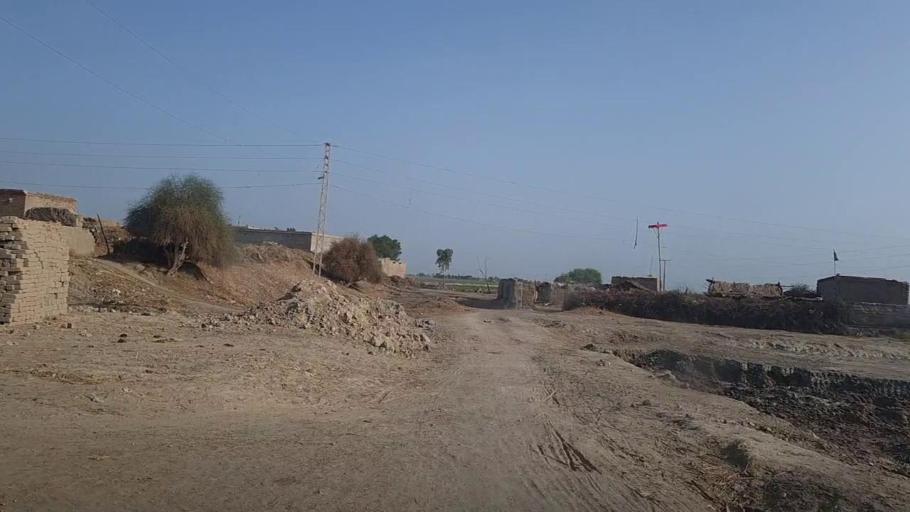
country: PK
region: Sindh
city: Sita Road
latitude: 27.1097
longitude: 67.8833
